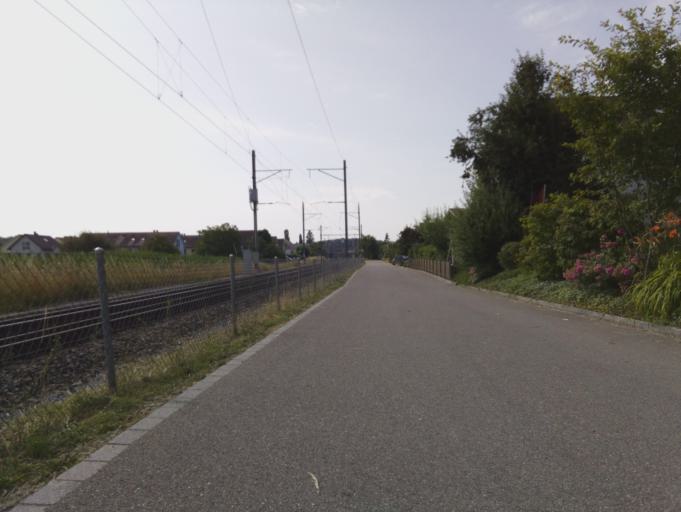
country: CH
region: Zurich
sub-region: Bezirk Andelfingen
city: Henggart
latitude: 47.5680
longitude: 8.6835
